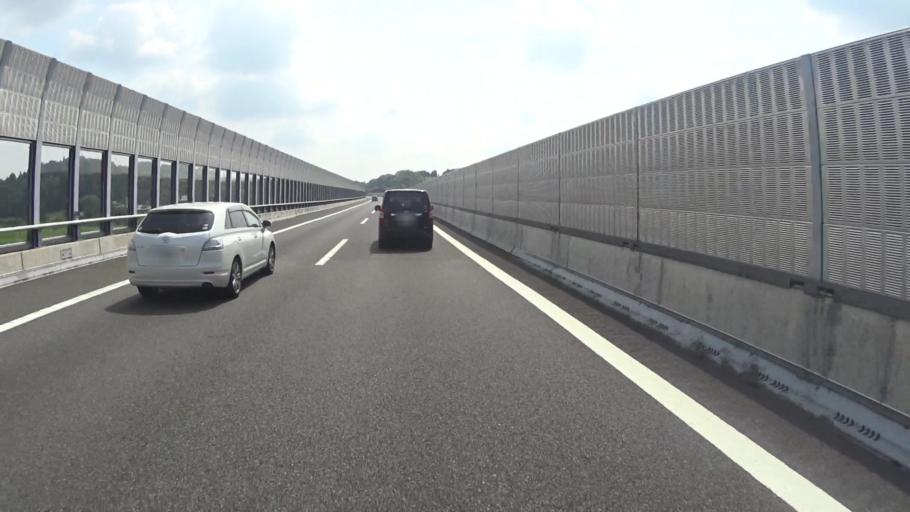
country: JP
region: Shiga Prefecture
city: Minakuchicho-matoba
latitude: 34.9126
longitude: 136.1936
